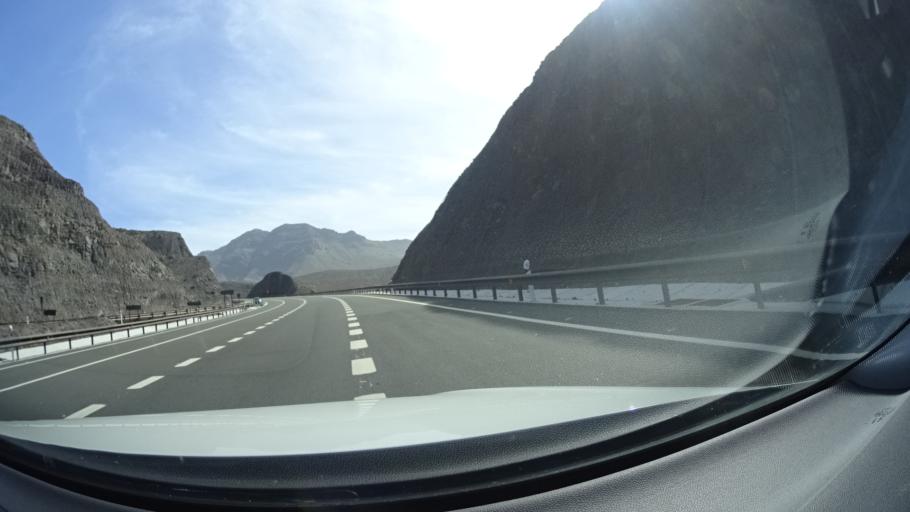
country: ES
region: Canary Islands
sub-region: Provincia de Las Palmas
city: San Nicolas
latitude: 28.0092
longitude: -15.7869
